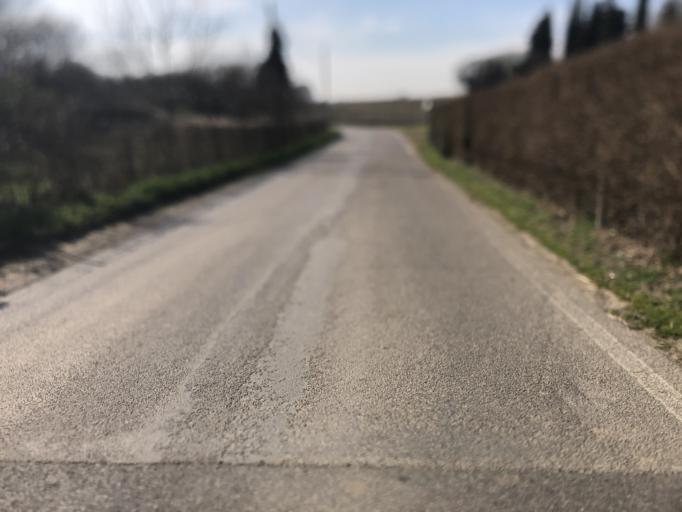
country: IT
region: Veneto
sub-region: Provincia di Verona
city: San Giorgio in Salici
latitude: 45.3987
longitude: 10.7729
